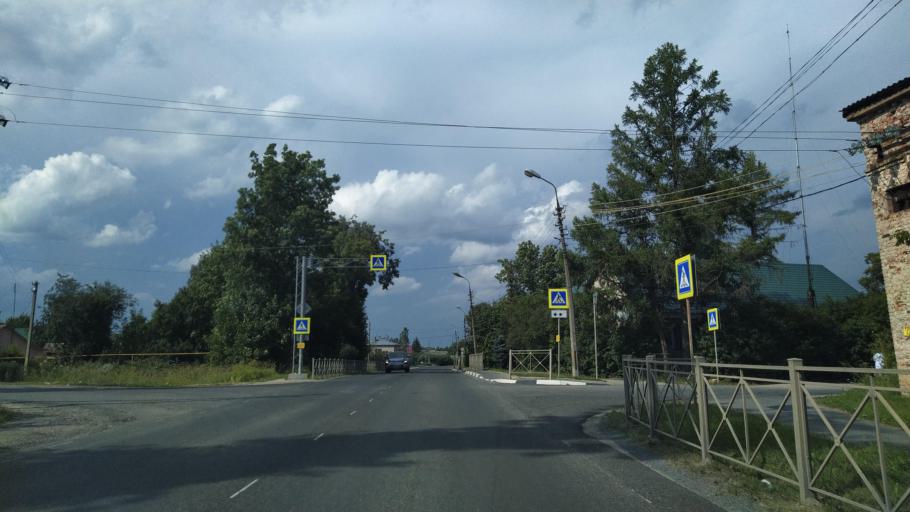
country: RU
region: Pskov
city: Porkhov
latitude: 57.7660
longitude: 29.5540
